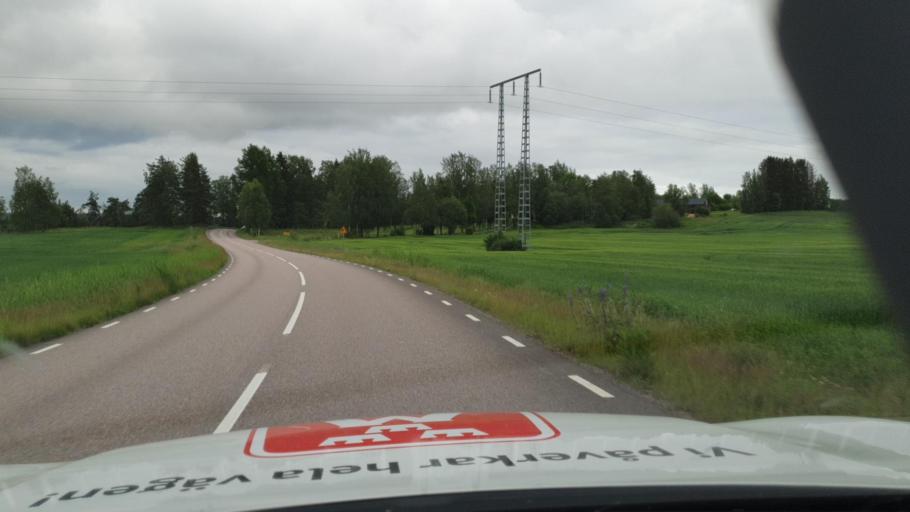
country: SE
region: Vaermland
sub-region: Kils Kommun
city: Kil
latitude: 59.5139
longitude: 13.3840
